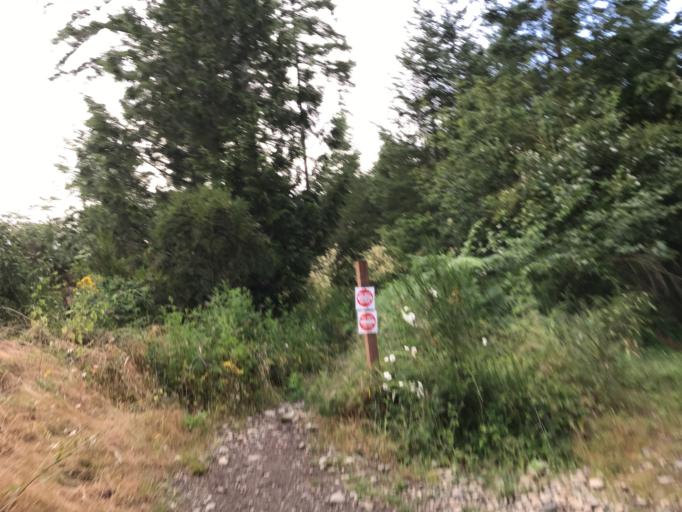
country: US
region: Washington
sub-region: King County
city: Ravensdale
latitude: 47.3411
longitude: -122.0061
